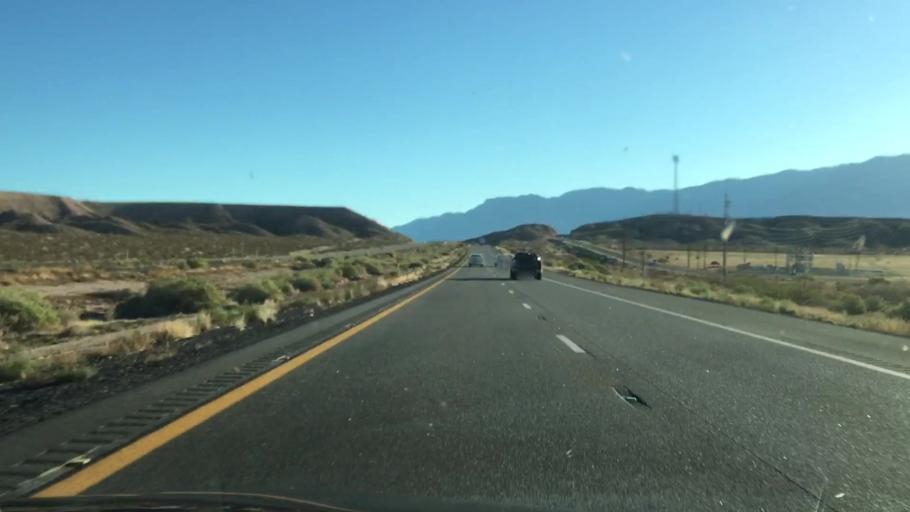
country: US
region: Nevada
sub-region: Clark County
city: Mesquite
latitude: 36.8277
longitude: -114.0145
